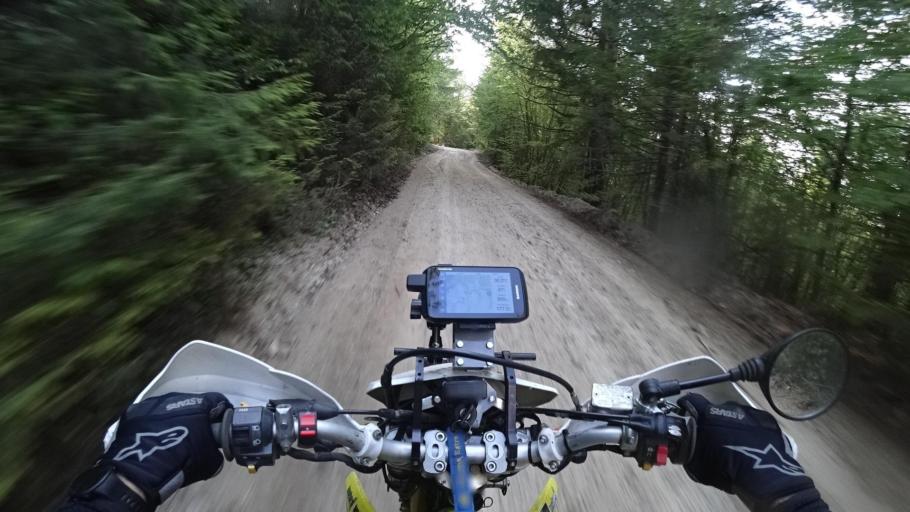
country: BA
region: Federation of Bosnia and Herzegovina
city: Glamoc
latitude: 44.0694
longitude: 16.7728
